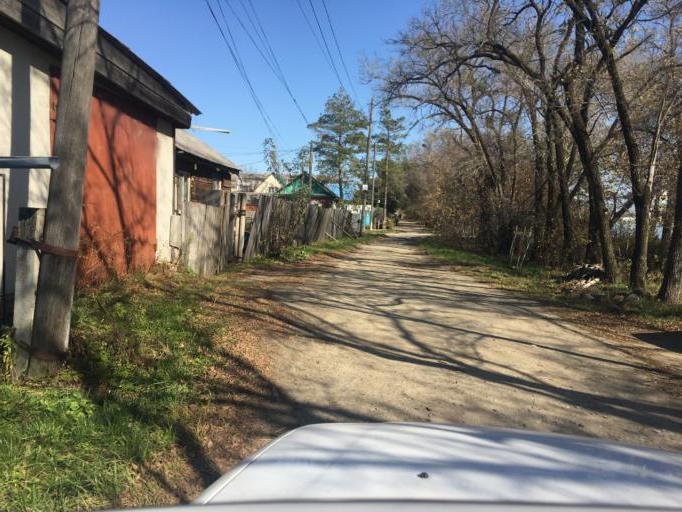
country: RU
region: Primorskiy
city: Dal'nerechensk
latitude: 45.9291
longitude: 133.7397
